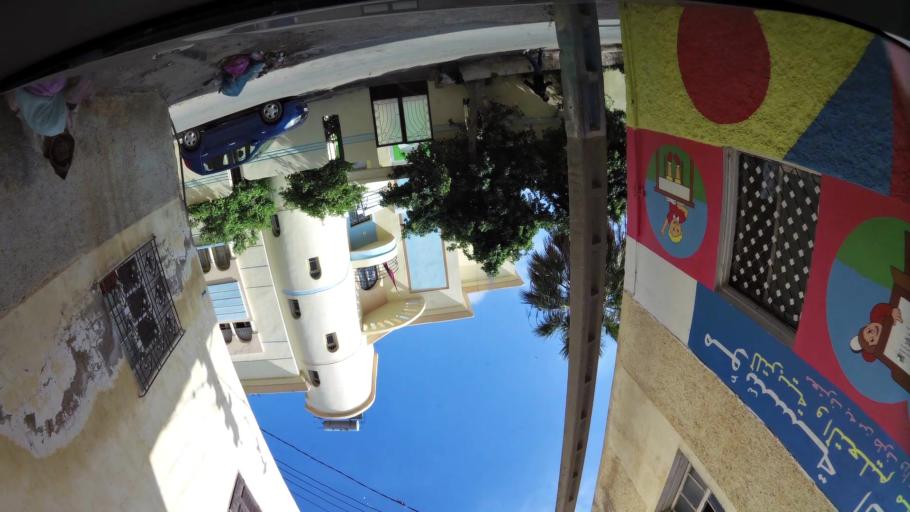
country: MA
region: Fes-Boulemane
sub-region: Fes
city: Fes
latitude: 34.0656
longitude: -5.0090
